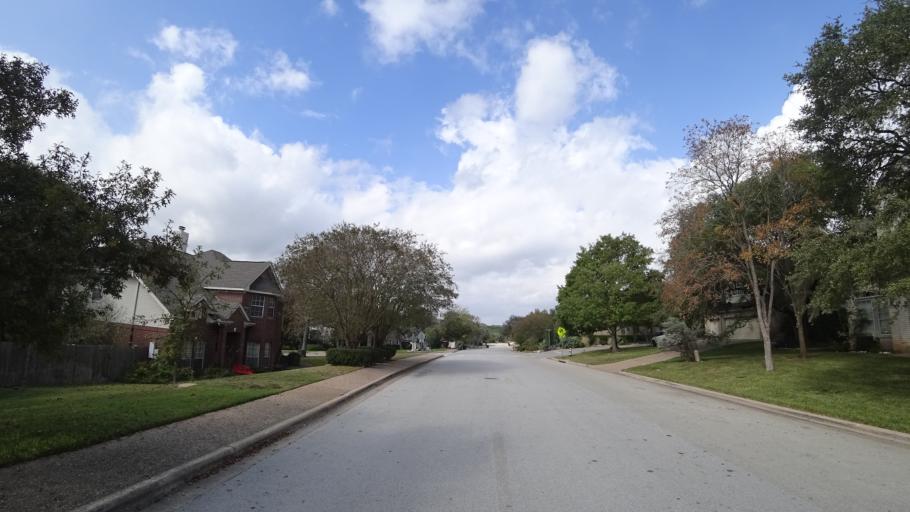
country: US
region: Texas
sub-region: Travis County
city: Barton Creek
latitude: 30.3016
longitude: -97.8860
